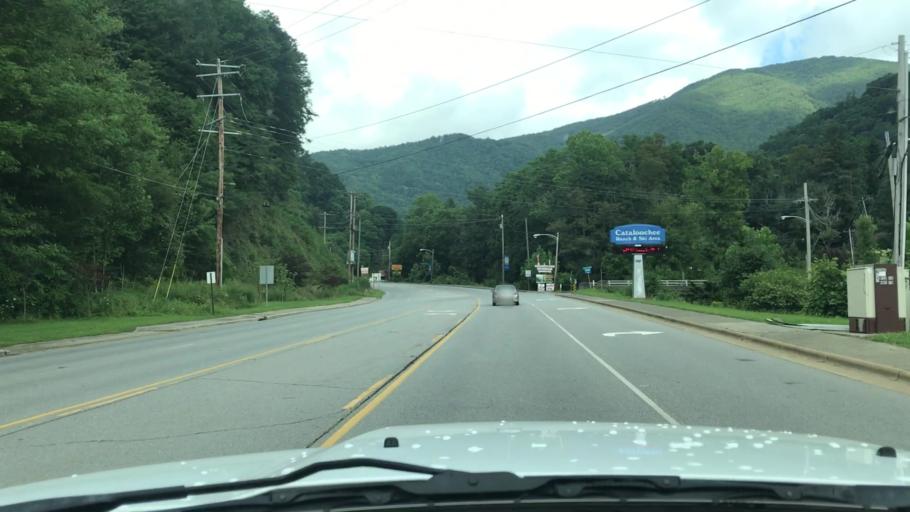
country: US
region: North Carolina
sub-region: Haywood County
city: Maggie Valley
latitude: 35.5205
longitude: -83.1073
